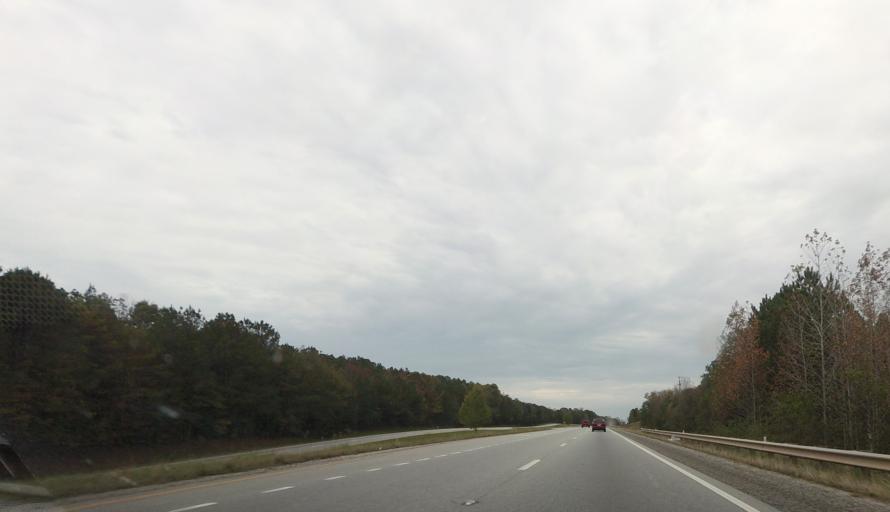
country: US
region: Alabama
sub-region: Lee County
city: Opelika
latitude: 32.6373
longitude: -85.3056
